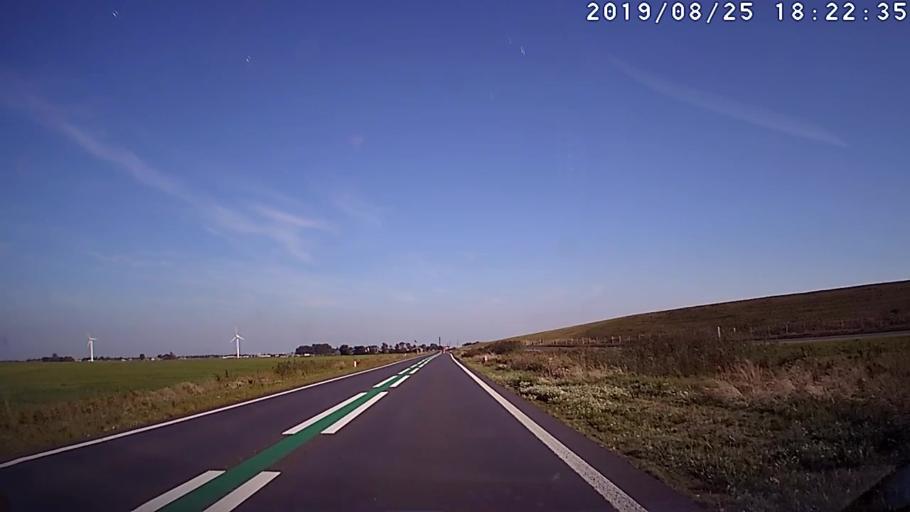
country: NL
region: Friesland
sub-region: Gemeente Lemsterland
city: Lemmer
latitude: 52.8641
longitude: 5.6512
